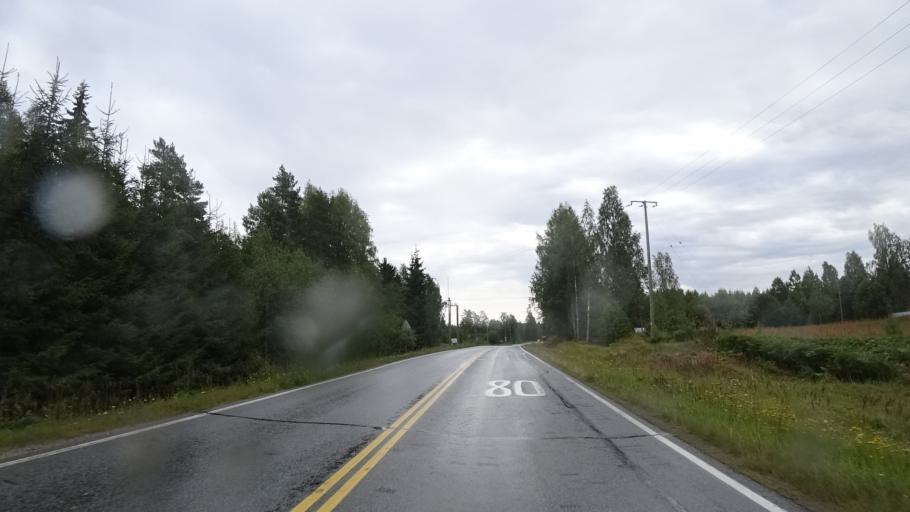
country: FI
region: North Karelia
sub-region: Keski-Karjala
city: Kesaelahti
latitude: 62.1057
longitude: 29.8262
